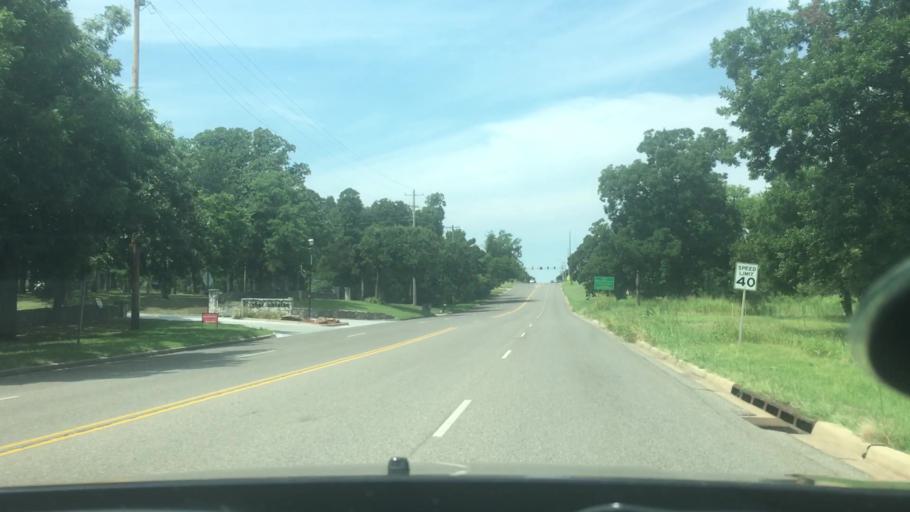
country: US
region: Oklahoma
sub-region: Pottawatomie County
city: Shawnee
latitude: 35.3327
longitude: -96.8899
